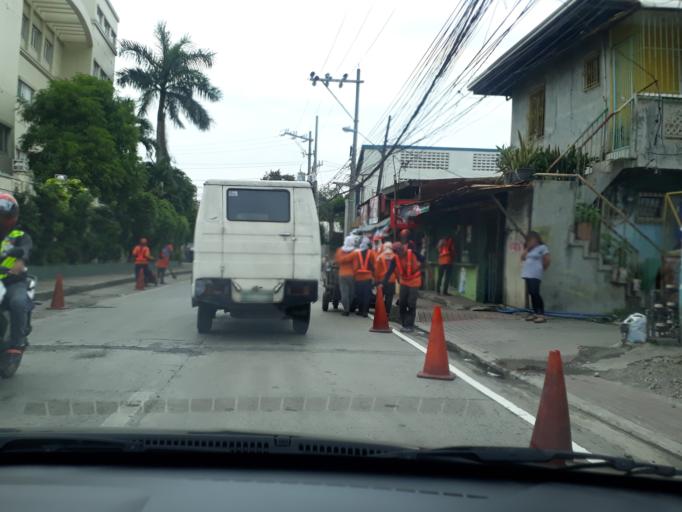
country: PH
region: Calabarzon
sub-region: Province of Rizal
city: Valenzuela
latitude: 14.7152
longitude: 120.9808
